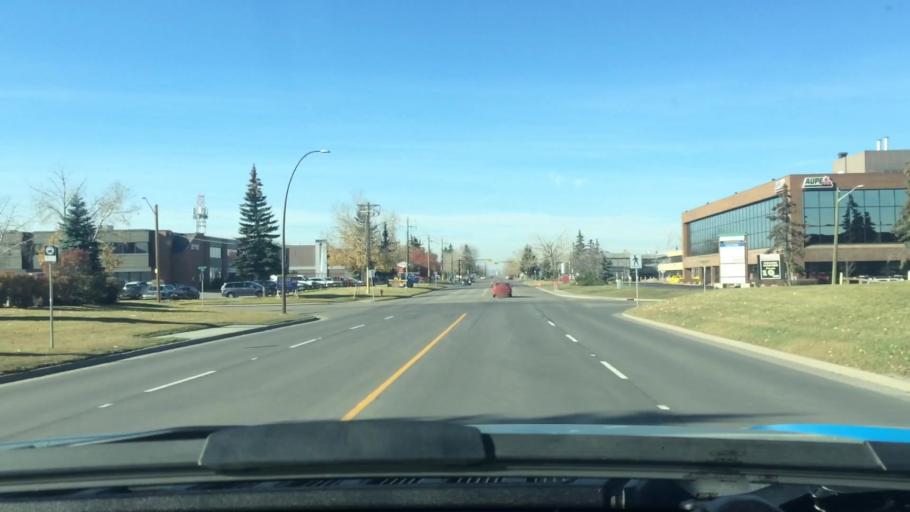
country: CA
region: Alberta
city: Calgary
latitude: 51.0769
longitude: -114.0081
